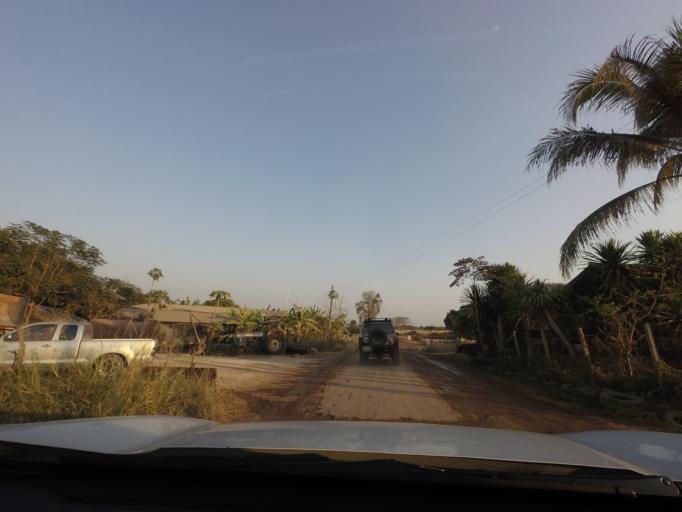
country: TH
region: Nakhon Ratchasima
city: Pak Chong
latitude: 14.6450
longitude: 101.4020
